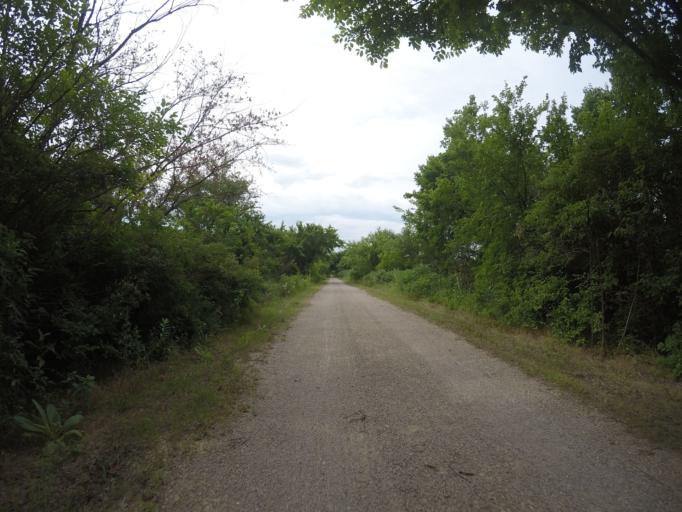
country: US
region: Kansas
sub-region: Franklin County
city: Ottawa
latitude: 38.5175
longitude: -95.2724
